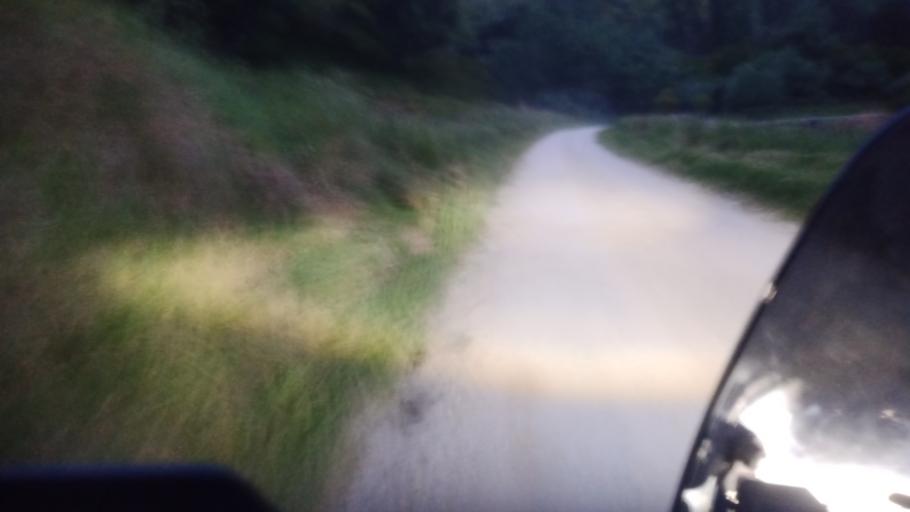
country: NZ
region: Gisborne
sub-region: Gisborne District
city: Gisborne
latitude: -38.4932
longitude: 177.9615
